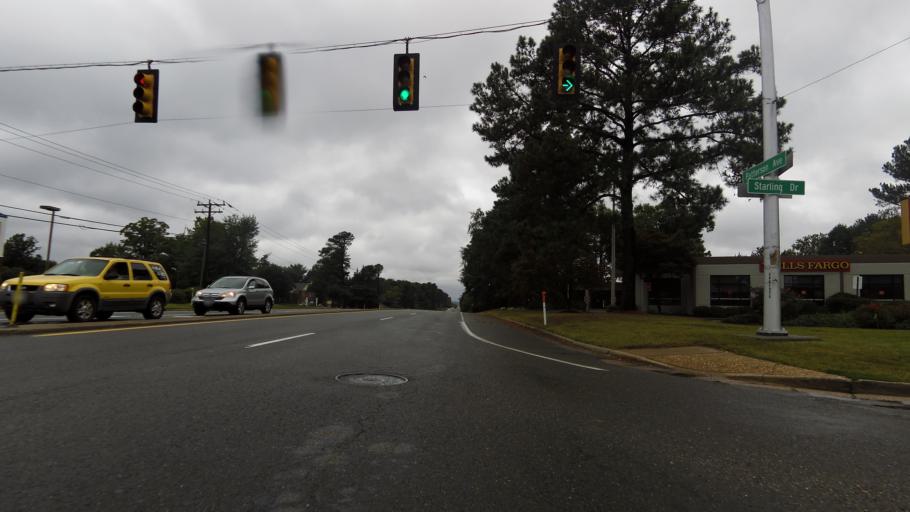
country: US
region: Virginia
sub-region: Henrico County
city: Tuckahoe
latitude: 37.5953
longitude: -77.5758
